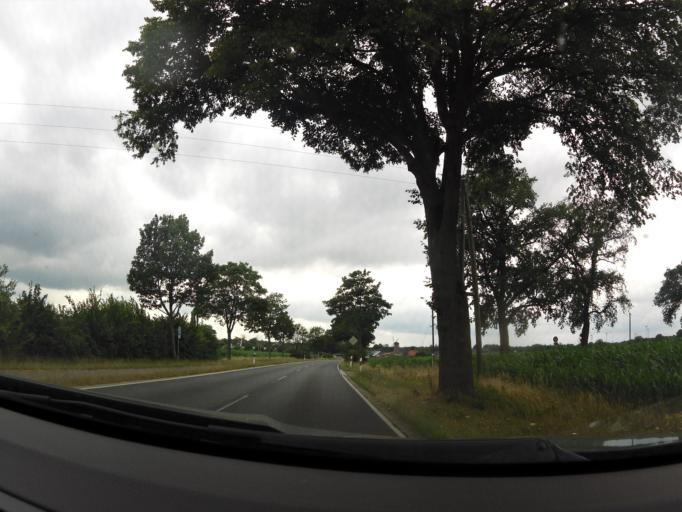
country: DE
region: North Rhine-Westphalia
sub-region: Regierungsbezirk Dusseldorf
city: Kevelaer
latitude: 51.5608
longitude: 6.2149
